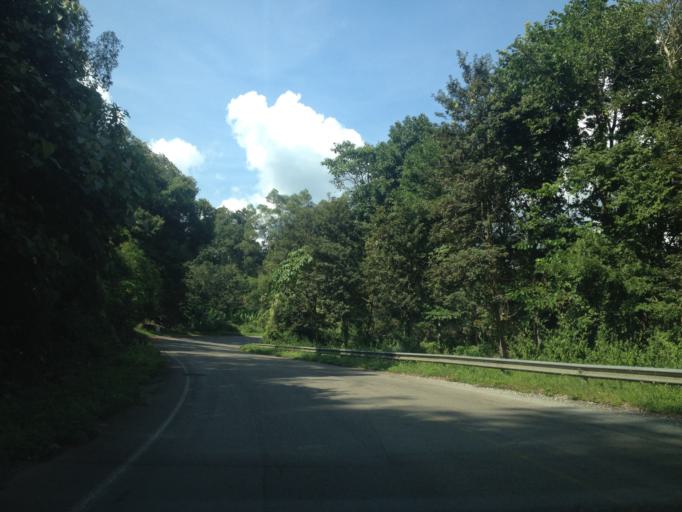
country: TH
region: Chiang Mai
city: Samoeng
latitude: 18.8094
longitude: 98.8181
